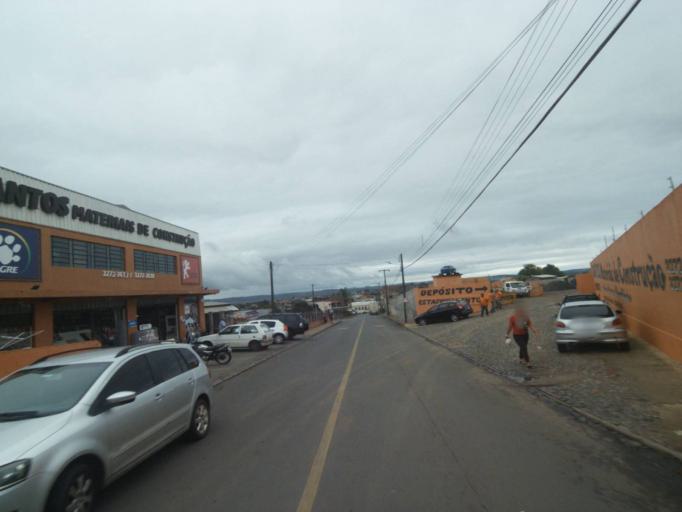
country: BR
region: Parana
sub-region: Telemaco Borba
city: Telemaco Borba
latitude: -24.3279
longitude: -50.6431
